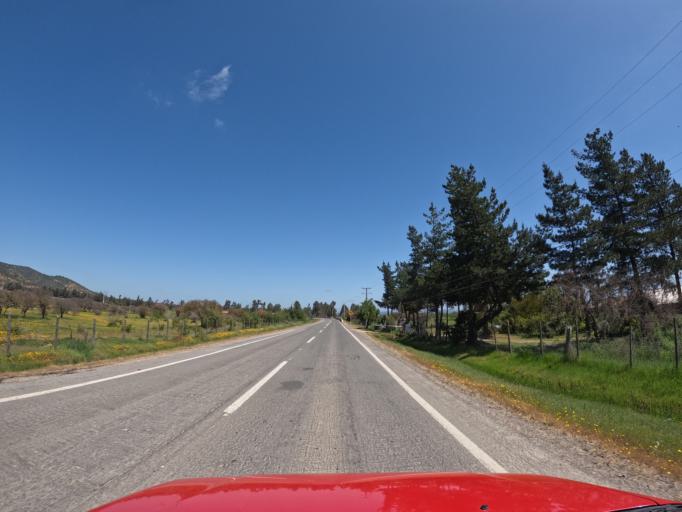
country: CL
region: O'Higgins
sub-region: Provincia de Colchagua
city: Santa Cruz
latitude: -34.7304
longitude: -71.6756
